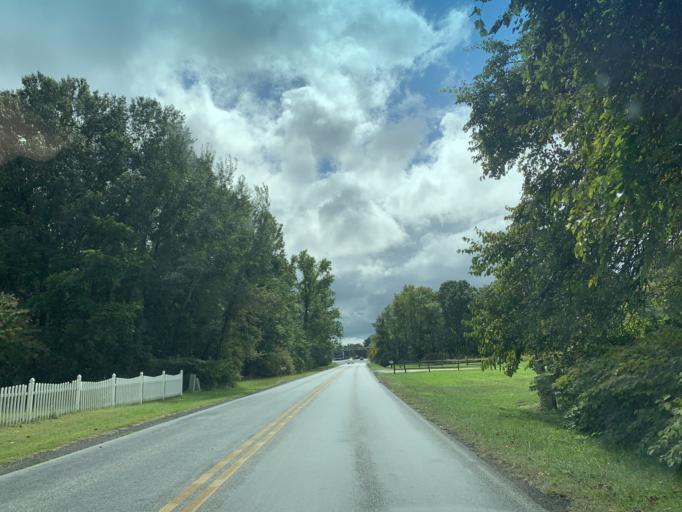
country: US
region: Maryland
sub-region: Caroline County
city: Denton
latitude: 38.8993
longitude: -75.8375
